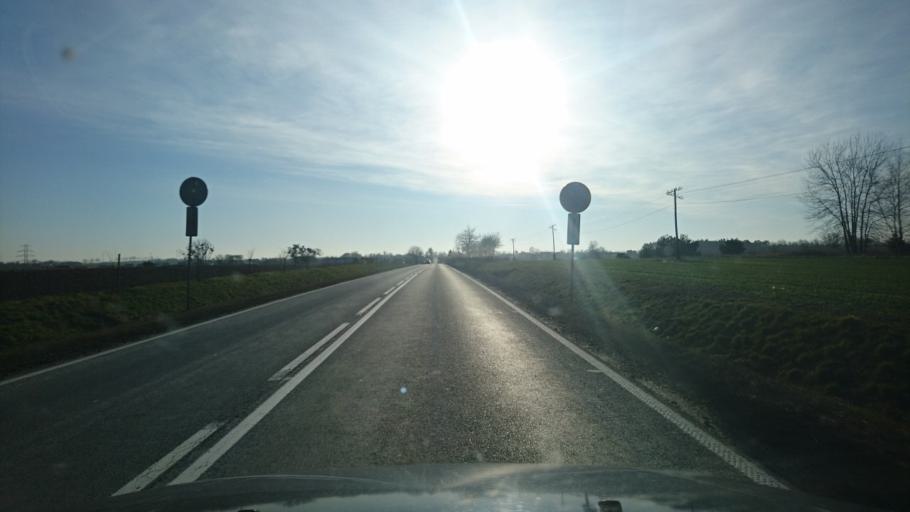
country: PL
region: Opole Voivodeship
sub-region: Powiat oleski
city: Dalachow
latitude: 51.0593
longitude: 18.5996
